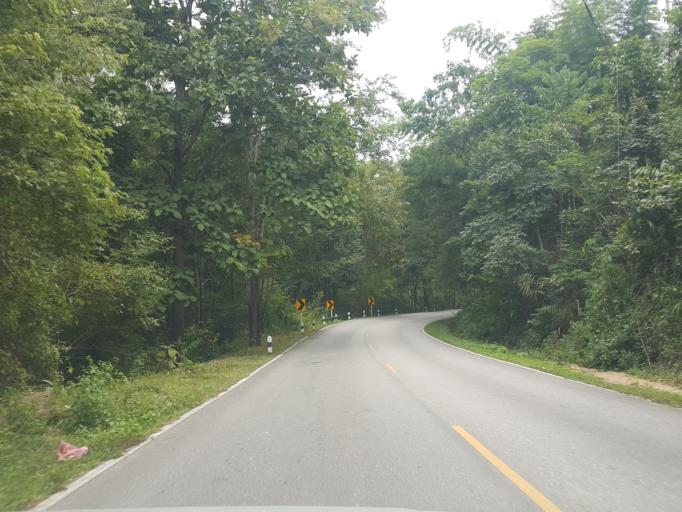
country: TH
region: Mae Hong Son
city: Mae Hi
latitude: 19.2794
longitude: 98.4921
